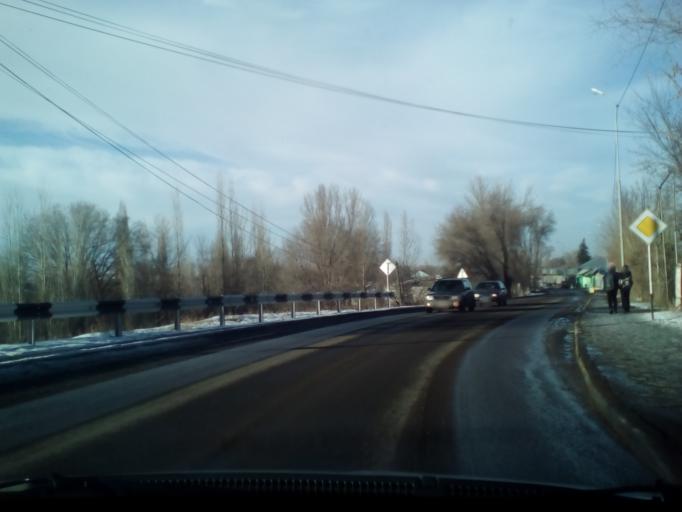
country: KZ
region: Almaty Oblysy
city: Burunday
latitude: 43.1601
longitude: 76.4169
